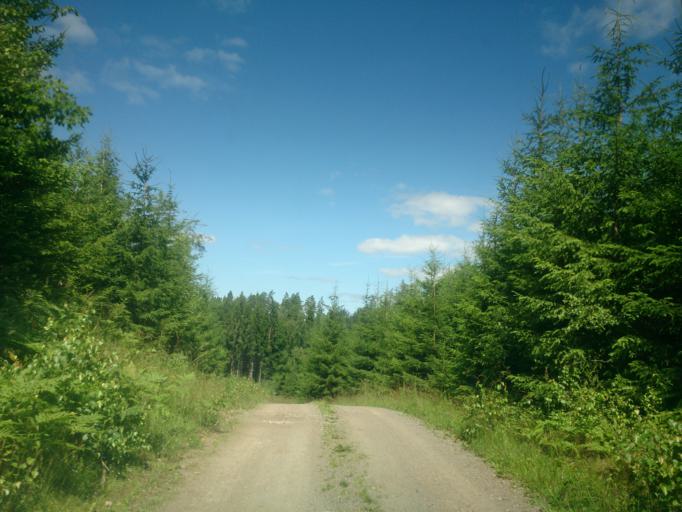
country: SE
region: OEstergoetland
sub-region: Atvidabergs Kommun
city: Atvidaberg
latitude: 58.2528
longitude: 16.0023
